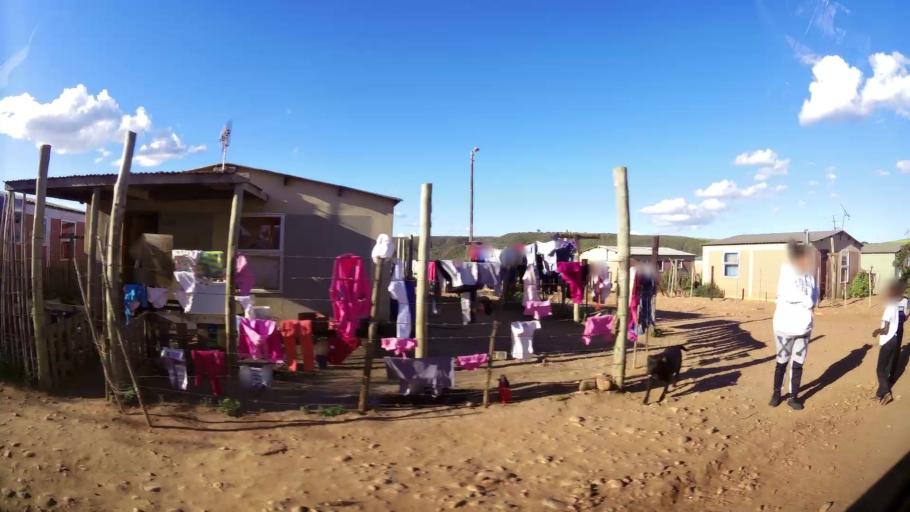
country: ZA
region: Western Cape
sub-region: Eden District Municipality
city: Riversdale
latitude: -34.1089
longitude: 20.9658
